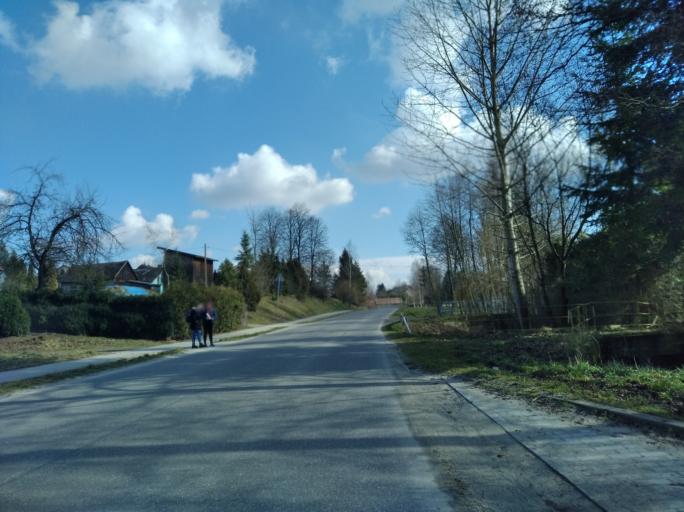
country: PL
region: Subcarpathian Voivodeship
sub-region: Powiat jasielski
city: Kolaczyce
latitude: 49.8531
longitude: 21.5009
